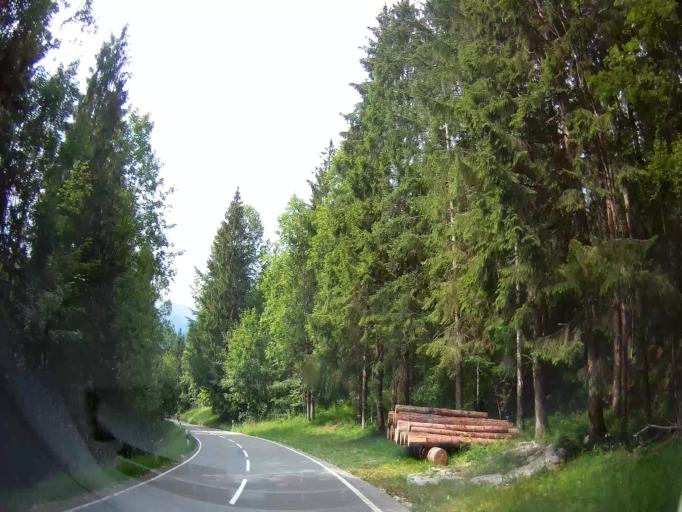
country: DE
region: Bavaria
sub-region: Upper Bavaria
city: Marktschellenberg
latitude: 47.6442
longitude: 13.0604
